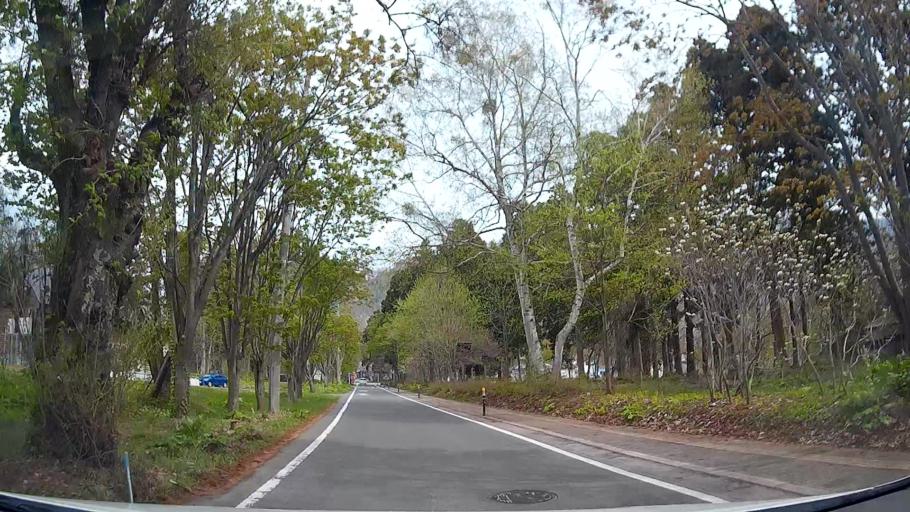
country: JP
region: Akita
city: Hanawa
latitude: 40.4266
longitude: 140.8954
